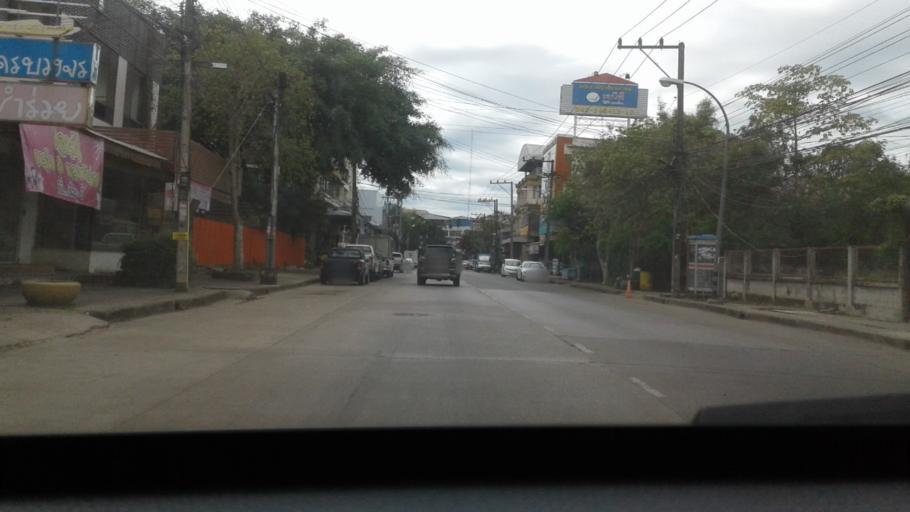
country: TH
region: Changwat Udon Thani
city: Udon Thani
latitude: 17.4069
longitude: 102.7978
